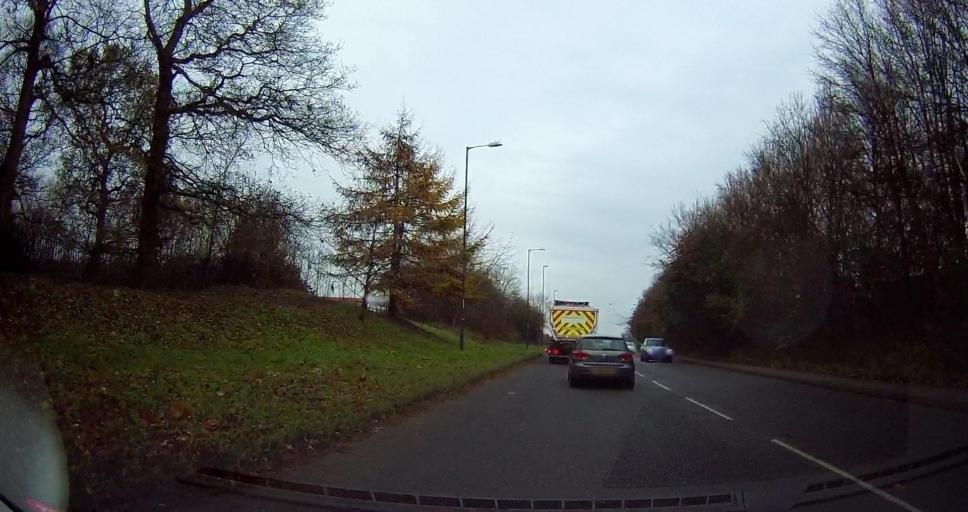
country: GB
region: England
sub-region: Nottinghamshire
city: Kimberley
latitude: 52.9741
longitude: -1.2340
